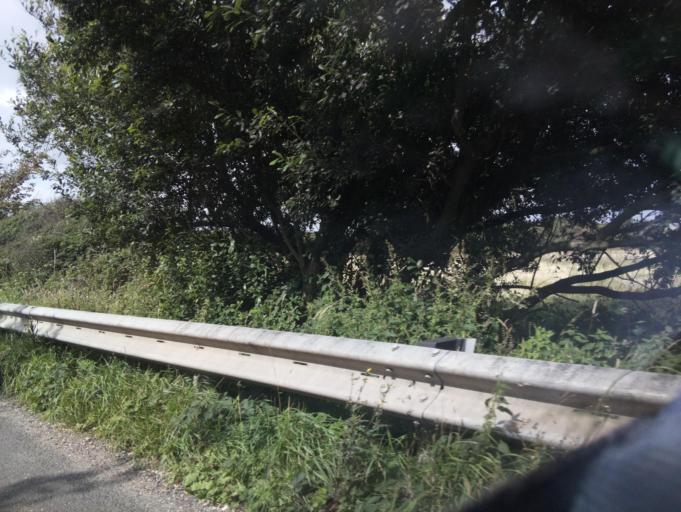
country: GB
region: England
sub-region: Hampshire
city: Milford on Sea
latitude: 50.7331
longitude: -1.6274
